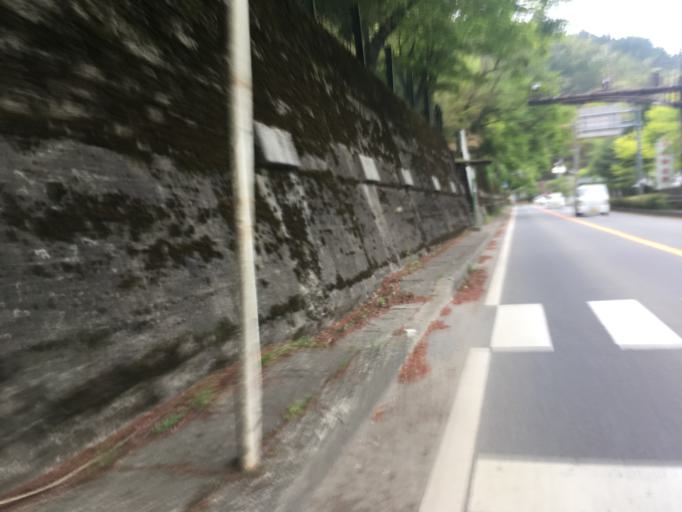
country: JP
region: Kyoto
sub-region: Kyoto-shi
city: Kamigyo-ku
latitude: 35.1207
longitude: 135.6528
